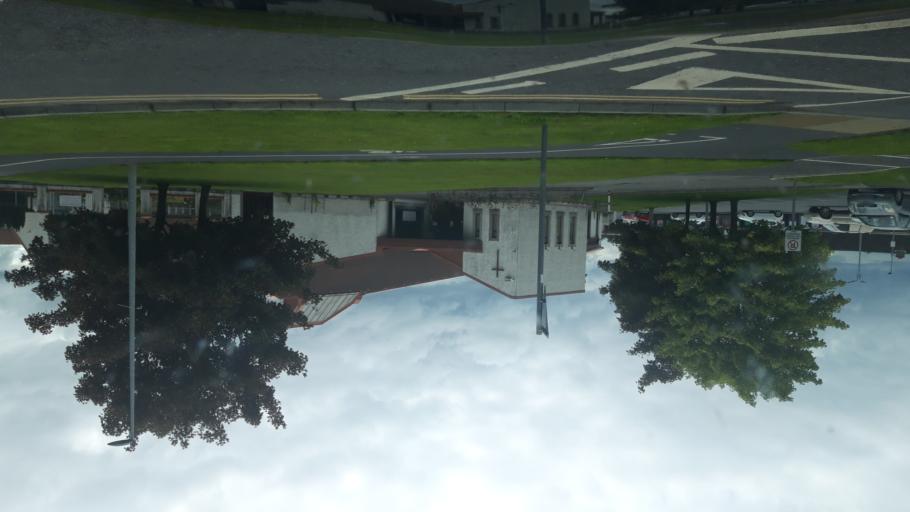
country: IE
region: Leinster
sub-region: Kilkenny
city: Kilkenny
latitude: 52.6407
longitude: -7.2425
